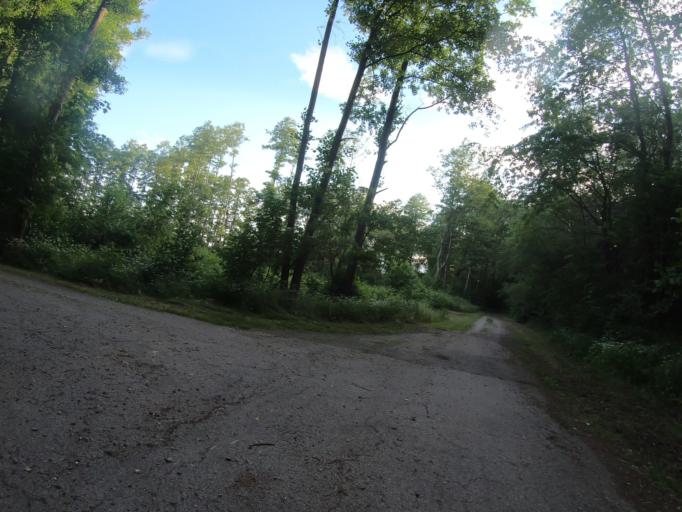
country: DE
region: Lower Saxony
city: Gifhorn
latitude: 52.4898
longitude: 10.5702
